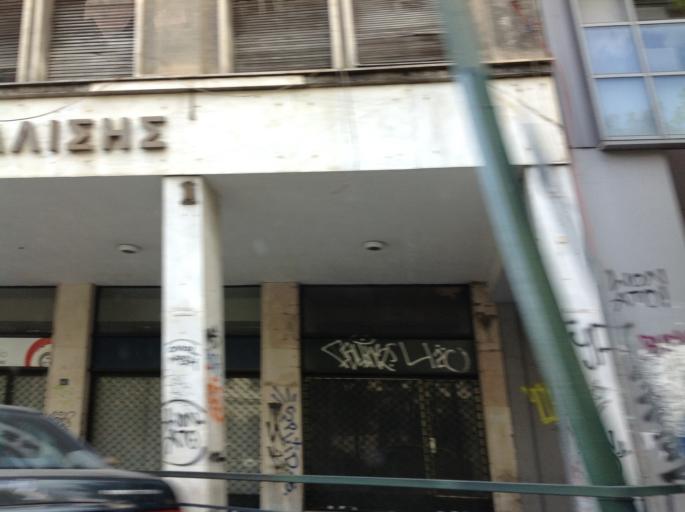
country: GR
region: Attica
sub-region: Nomarchia Athinas
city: Athens
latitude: 37.9823
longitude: 23.7238
